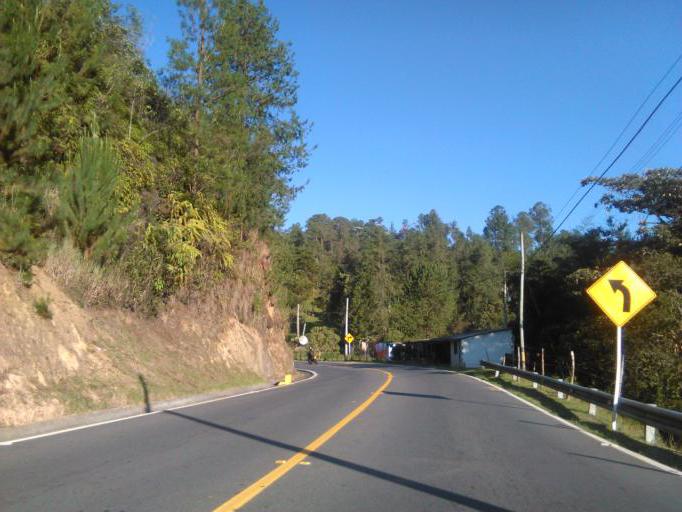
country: CO
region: Antioquia
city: El Retiro
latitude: 6.0722
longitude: -75.4661
